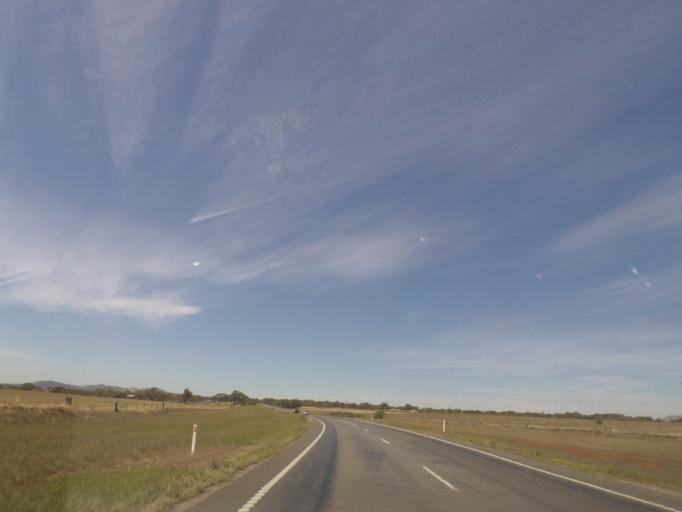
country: AU
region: Victoria
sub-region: Wyndham
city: Wyndham Vale
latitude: -37.8468
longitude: 144.3873
